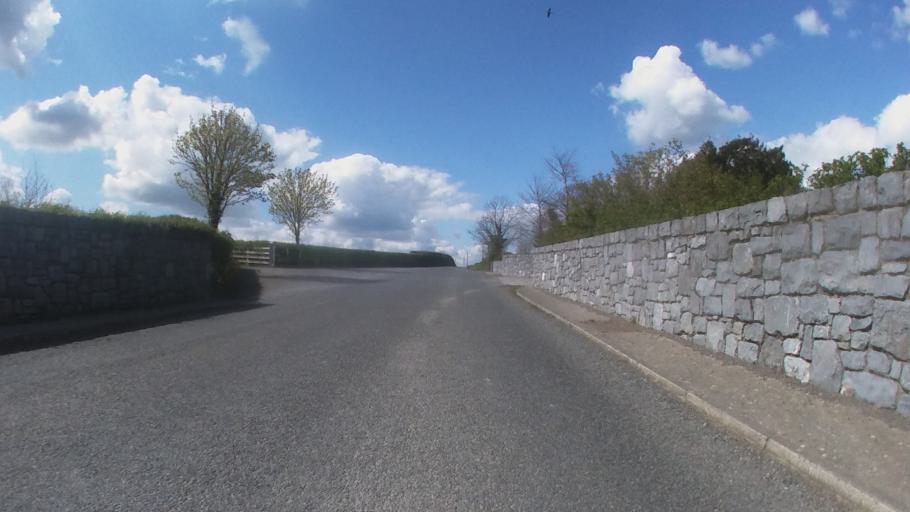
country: IE
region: Leinster
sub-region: Kilkenny
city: Kilkenny
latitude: 52.6613
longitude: -7.1956
